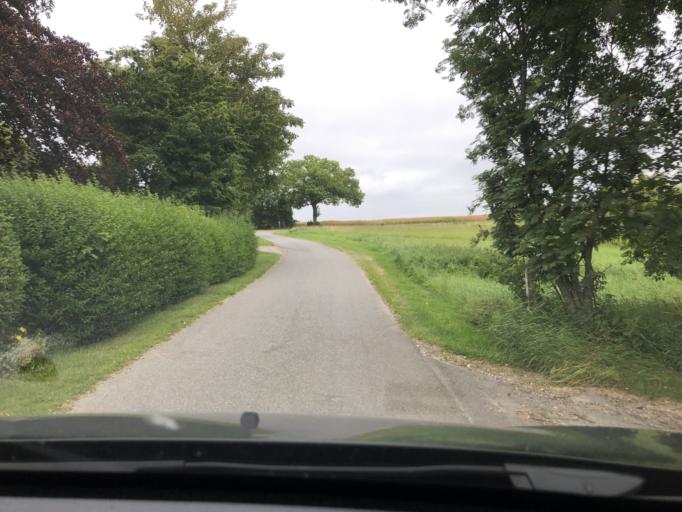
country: DK
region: South Denmark
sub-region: AEro Kommune
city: AEroskobing
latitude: 54.8338
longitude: 10.4249
